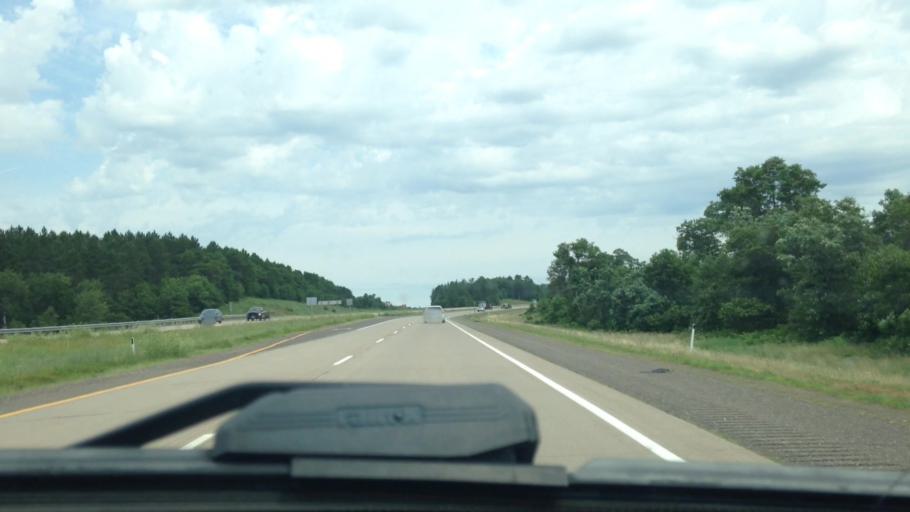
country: US
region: Wisconsin
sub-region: Douglas County
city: Lake Nebagamon
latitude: 46.2014
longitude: -91.7995
